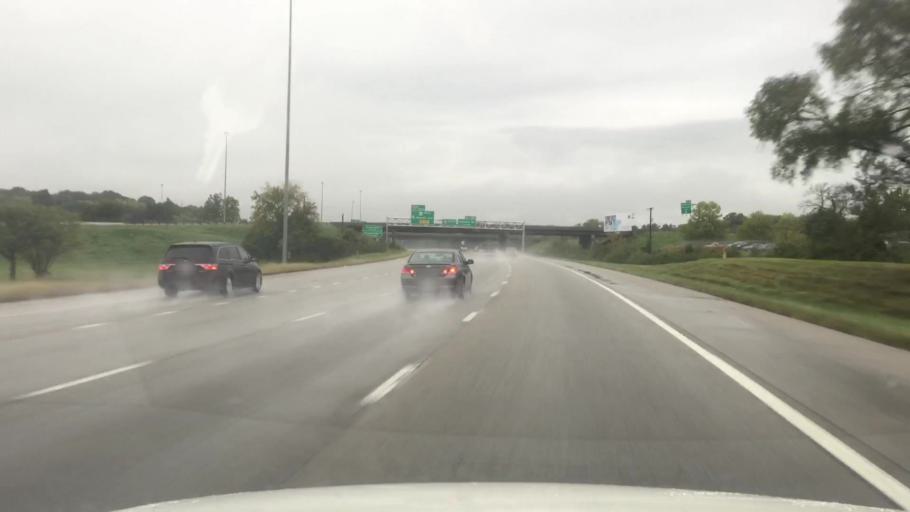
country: US
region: Kansas
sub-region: Johnson County
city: Mission
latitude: 39.0420
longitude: -94.6701
